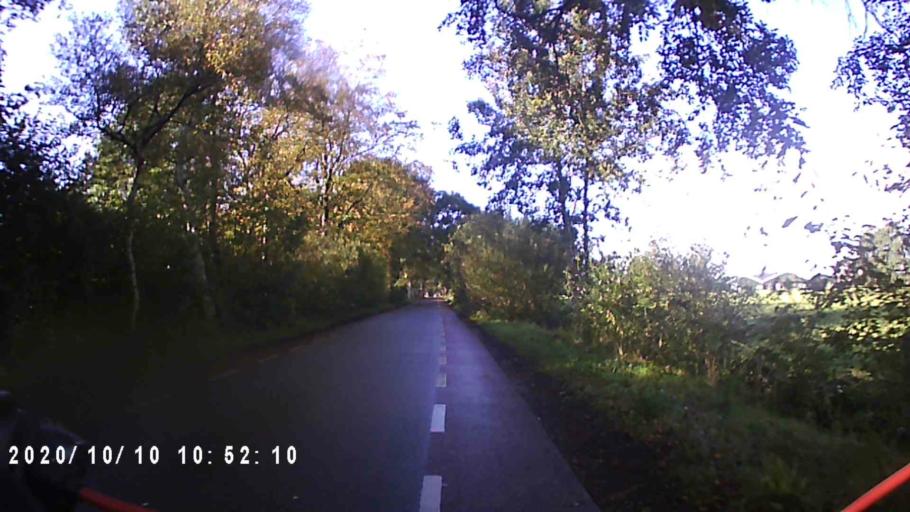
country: NL
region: Friesland
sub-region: Gemeente Achtkarspelen
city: Surhuisterveen
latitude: 53.1585
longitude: 6.2248
